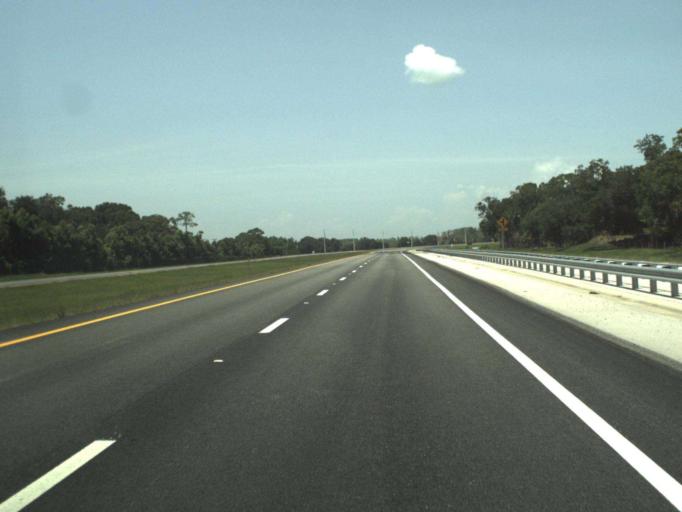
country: US
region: Florida
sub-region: Okeechobee County
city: Taylor Creek
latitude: 27.3154
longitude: -80.6570
